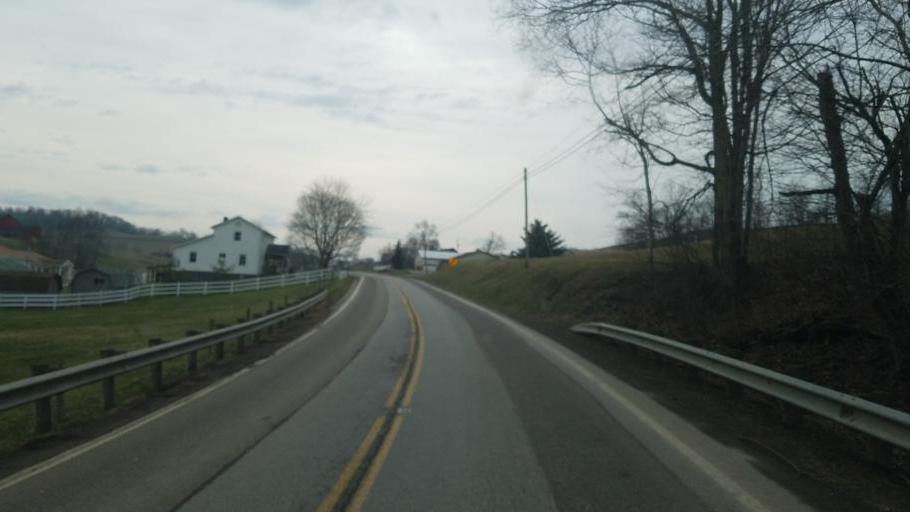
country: US
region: Ohio
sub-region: Holmes County
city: Millersburg
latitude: 40.5154
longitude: -81.8016
